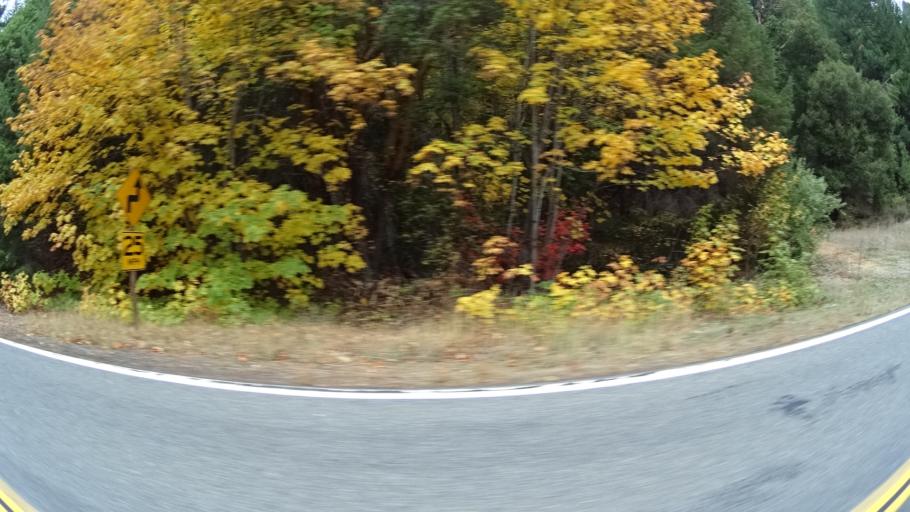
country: US
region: California
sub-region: Siskiyou County
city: Happy Camp
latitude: 41.9087
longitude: -123.4455
